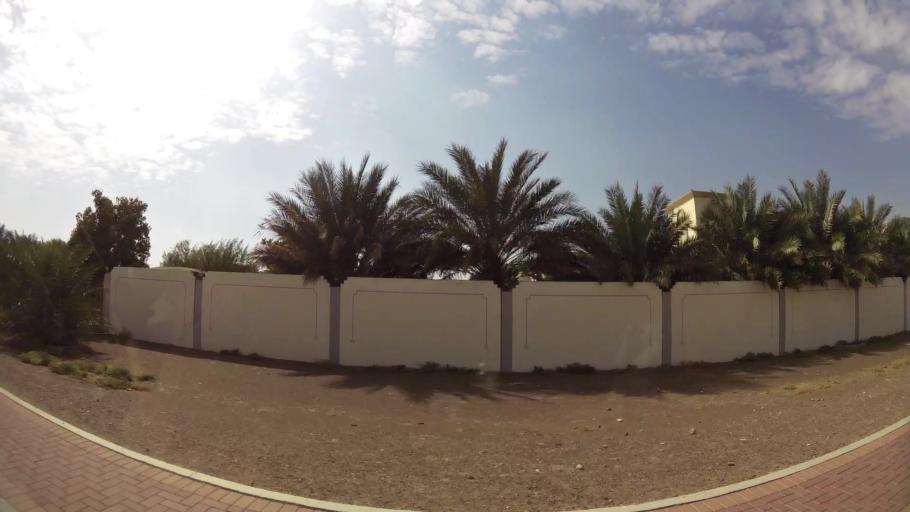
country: AE
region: Abu Dhabi
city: Al Ain
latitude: 24.0966
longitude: 55.9006
